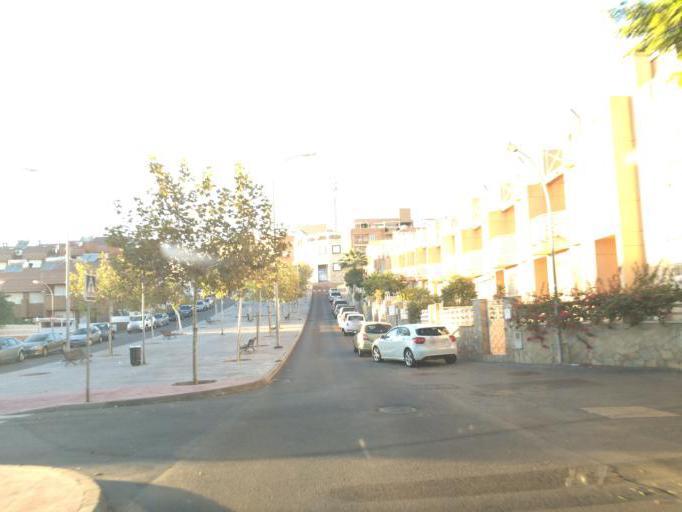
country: ES
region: Andalusia
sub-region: Provincia de Almeria
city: Almeria
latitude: 36.8533
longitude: -2.4415
